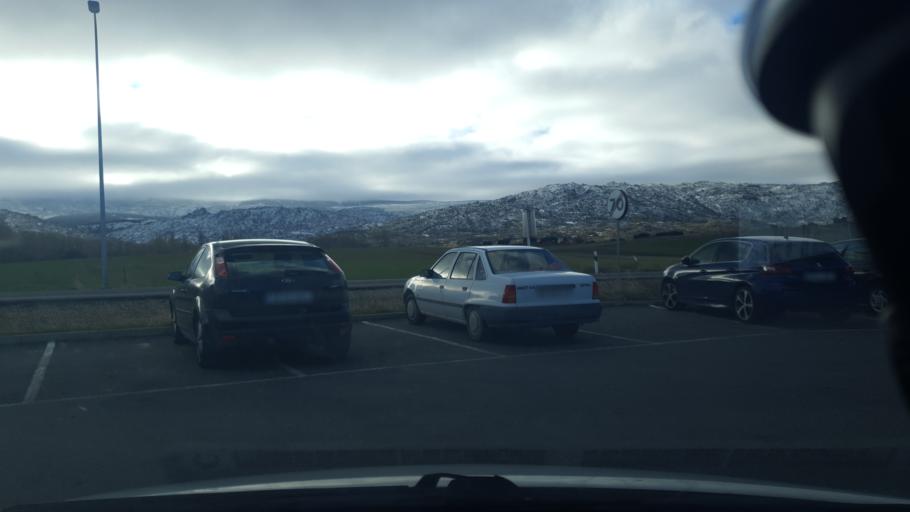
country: ES
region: Castille and Leon
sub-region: Provincia de Avila
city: Solosancho
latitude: 40.5533
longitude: -4.9092
